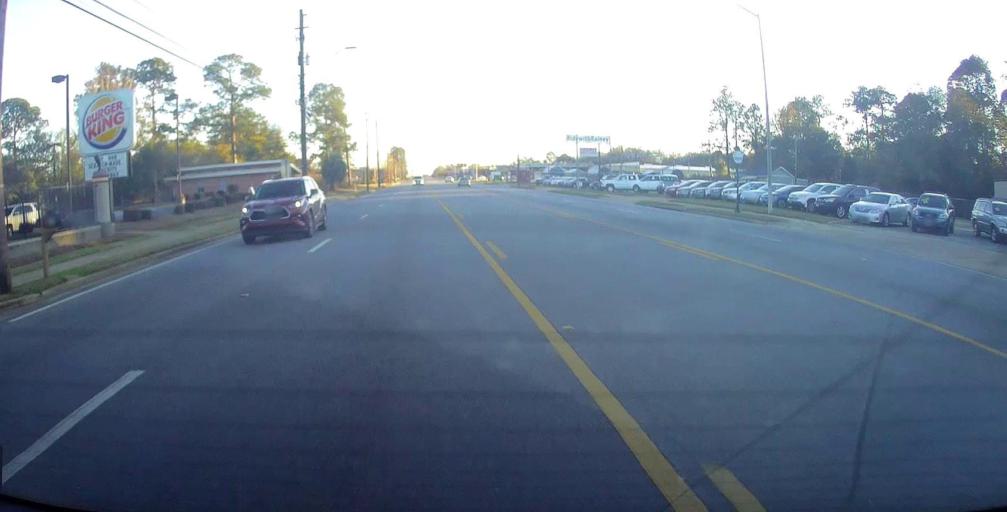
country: US
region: Georgia
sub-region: Dougherty County
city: Albany
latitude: 31.5664
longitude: -84.1762
